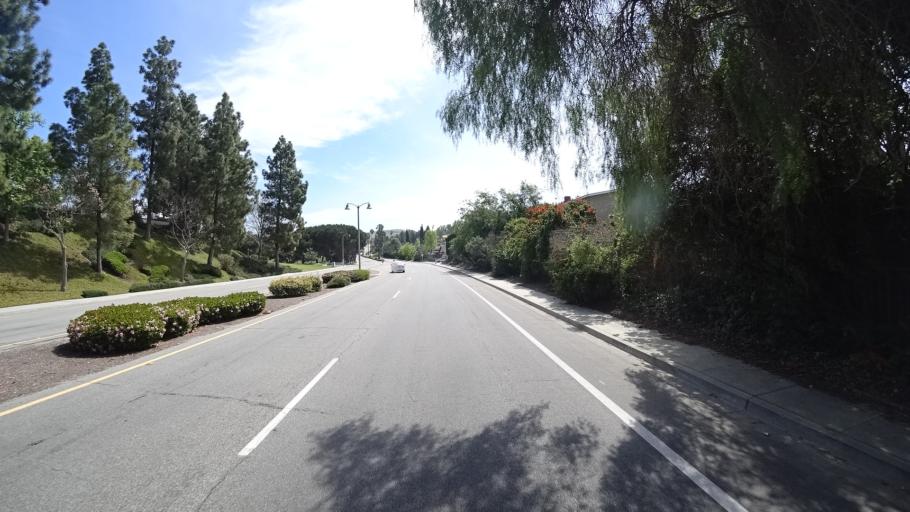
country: US
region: California
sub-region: Ventura County
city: Moorpark
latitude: 34.2315
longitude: -118.8565
